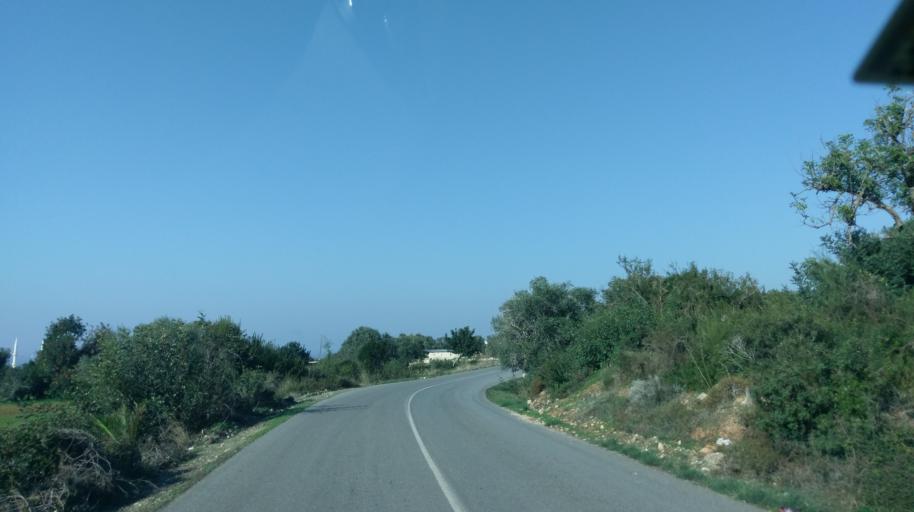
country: CY
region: Ammochostos
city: Leonarisso
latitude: 35.5282
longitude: 34.1932
